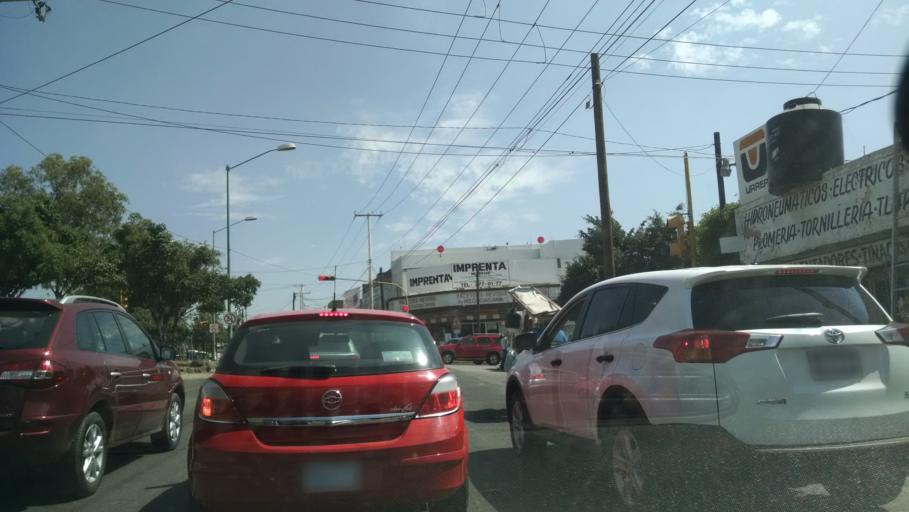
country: MX
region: Guanajuato
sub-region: Leon
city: Ejido la Joya
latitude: 21.1196
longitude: -101.7178
